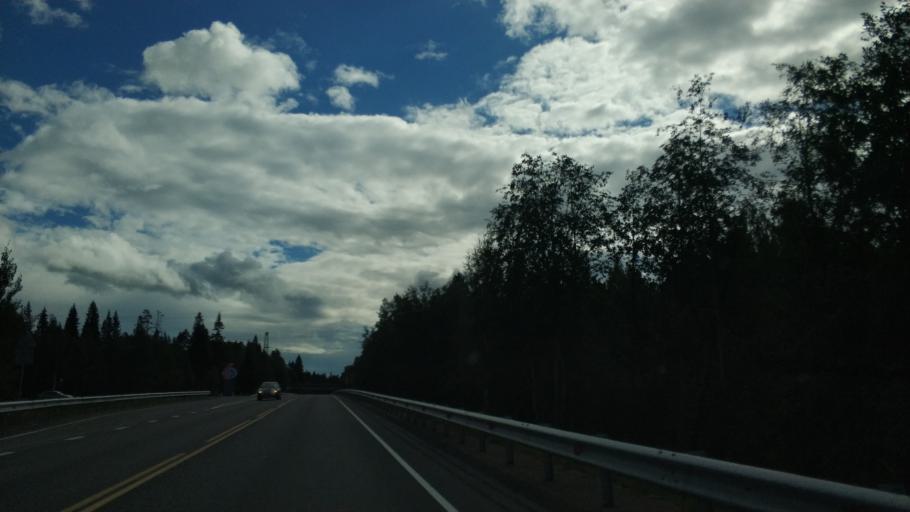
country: RU
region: Republic of Karelia
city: Khelyulya
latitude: 61.7817
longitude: 30.6575
